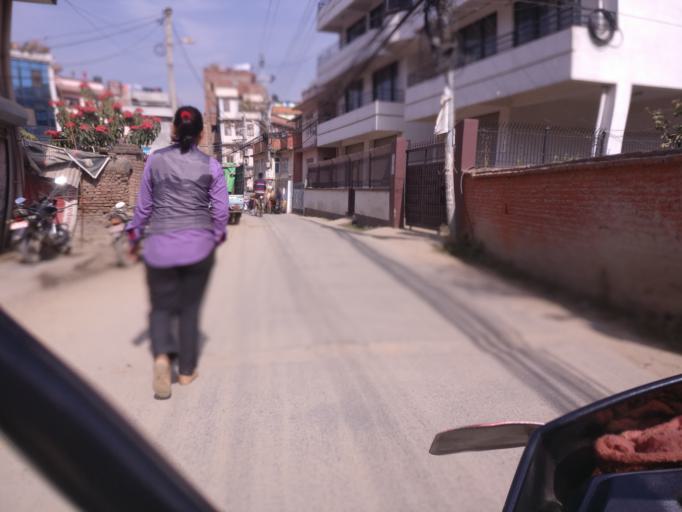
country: NP
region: Central Region
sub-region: Bagmati Zone
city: Patan
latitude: 27.6726
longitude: 85.3183
